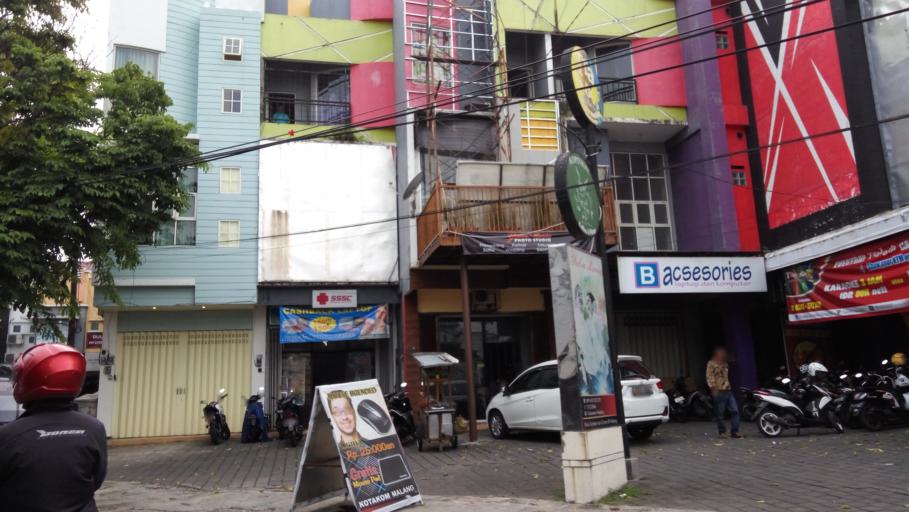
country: ID
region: East Java
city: Malang
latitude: -7.9536
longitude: 112.6103
